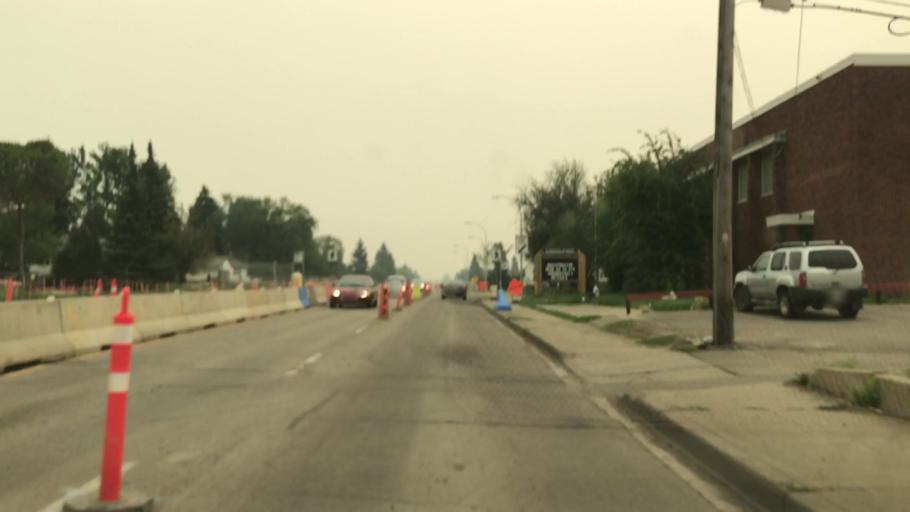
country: CA
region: Alberta
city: Edmonton
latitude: 53.5148
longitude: -113.4552
